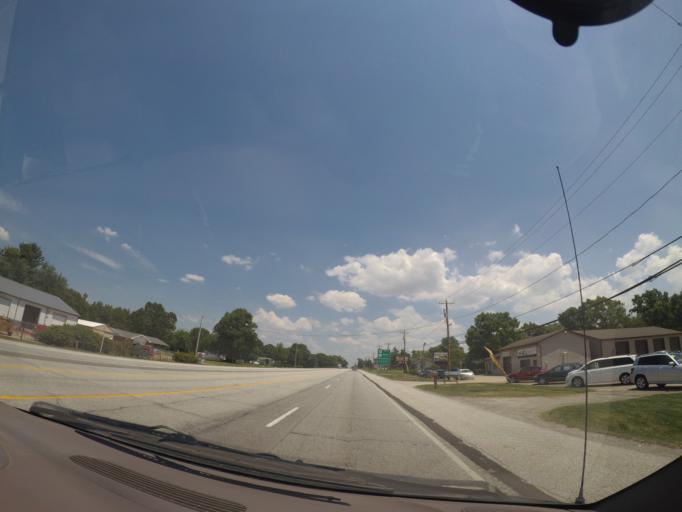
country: US
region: Indiana
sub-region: Saint Joseph County
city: South Bend
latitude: 41.6717
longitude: -86.3570
